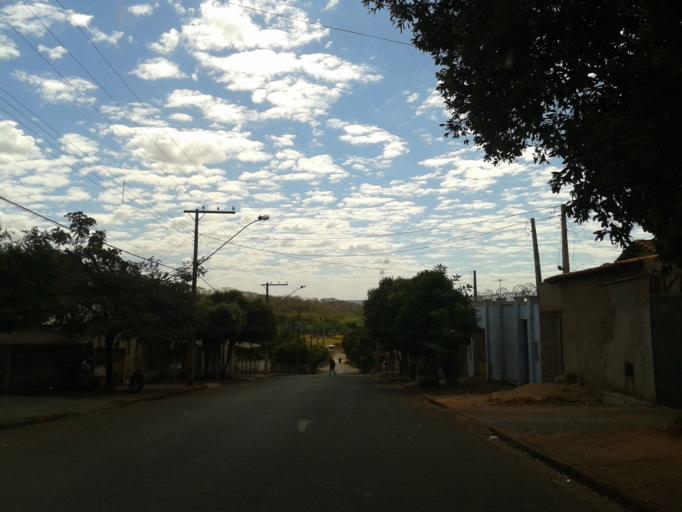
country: BR
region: Minas Gerais
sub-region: Ituiutaba
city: Ituiutaba
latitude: -18.9617
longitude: -49.4701
